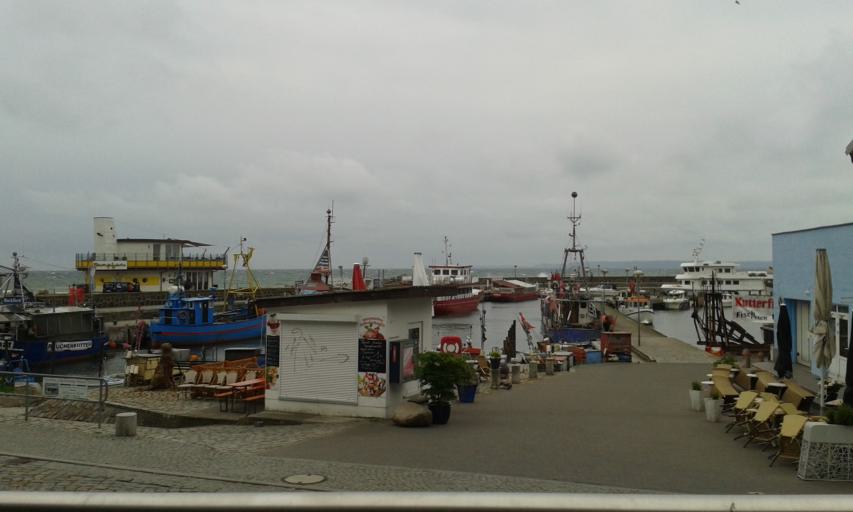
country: DE
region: Mecklenburg-Vorpommern
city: Sassnitz
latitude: 54.5154
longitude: 13.6500
